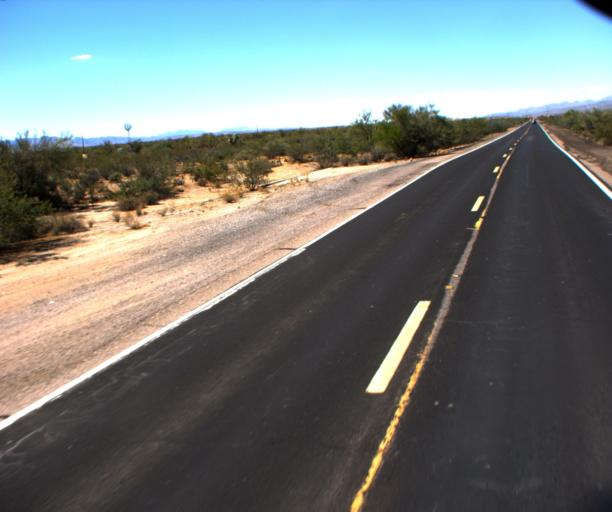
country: US
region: Arizona
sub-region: Yavapai County
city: Bagdad
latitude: 34.7206
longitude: -113.6148
